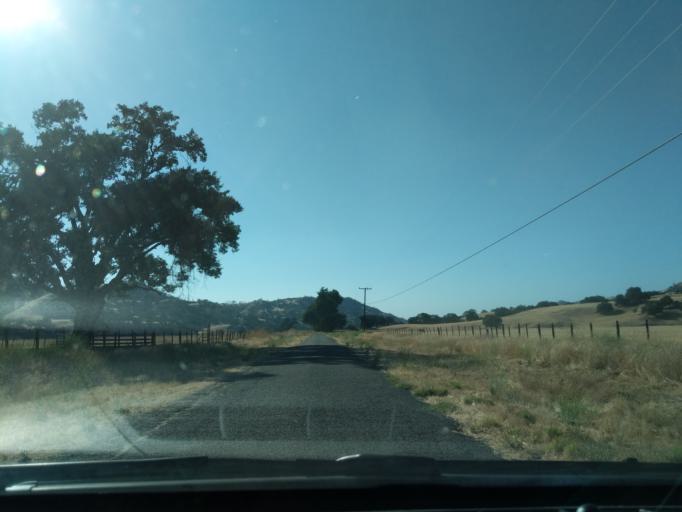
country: US
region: California
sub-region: San Luis Obispo County
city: San Miguel
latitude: 36.1145
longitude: -120.7244
